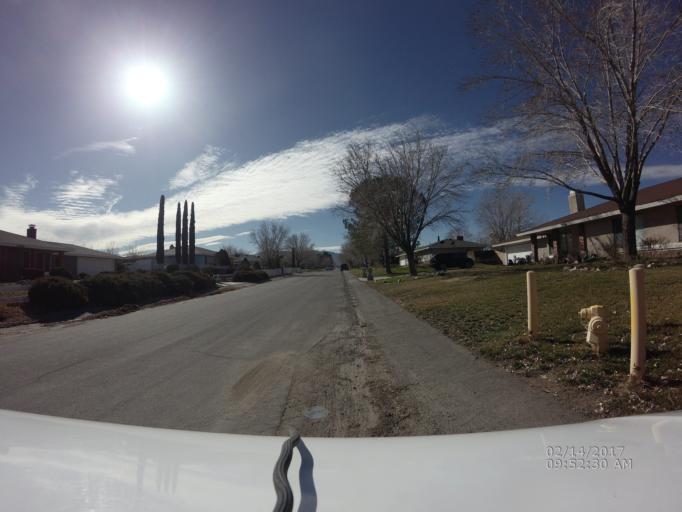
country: US
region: California
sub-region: Los Angeles County
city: Littlerock
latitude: 34.5558
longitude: -117.9598
